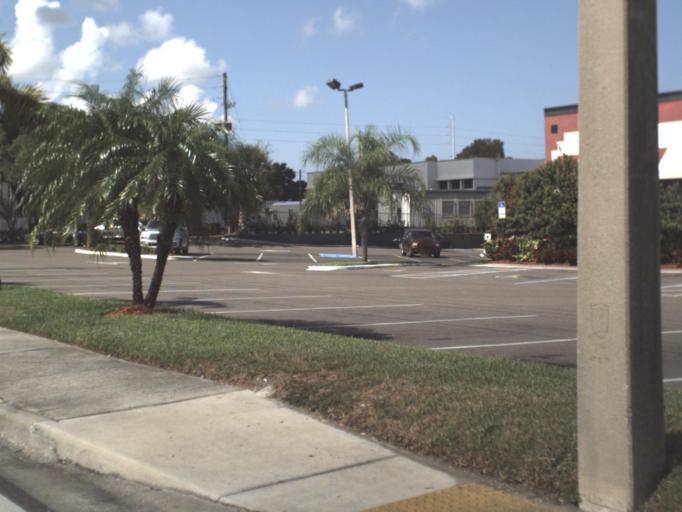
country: US
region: Florida
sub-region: Pinellas County
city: Clearwater
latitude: 27.9523
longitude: -82.7877
